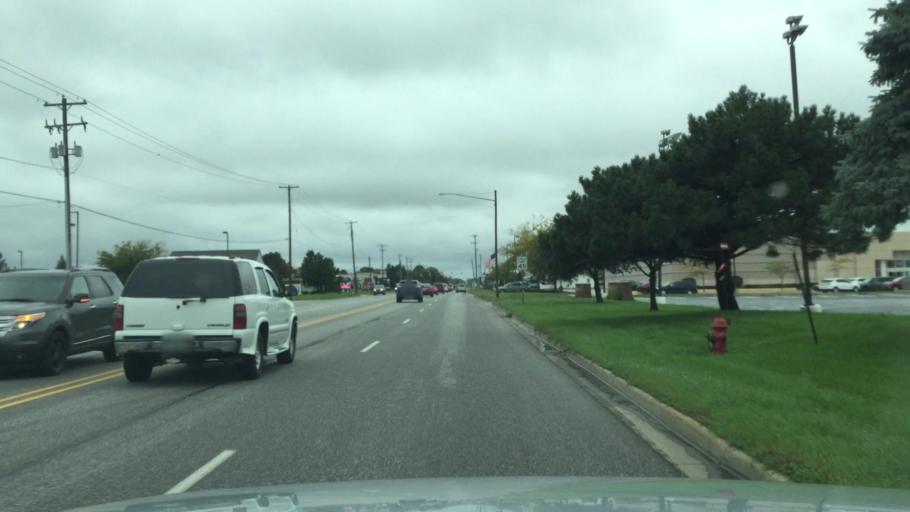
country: US
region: Michigan
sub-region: Saginaw County
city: Carrollton
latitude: 43.4801
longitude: -83.9758
